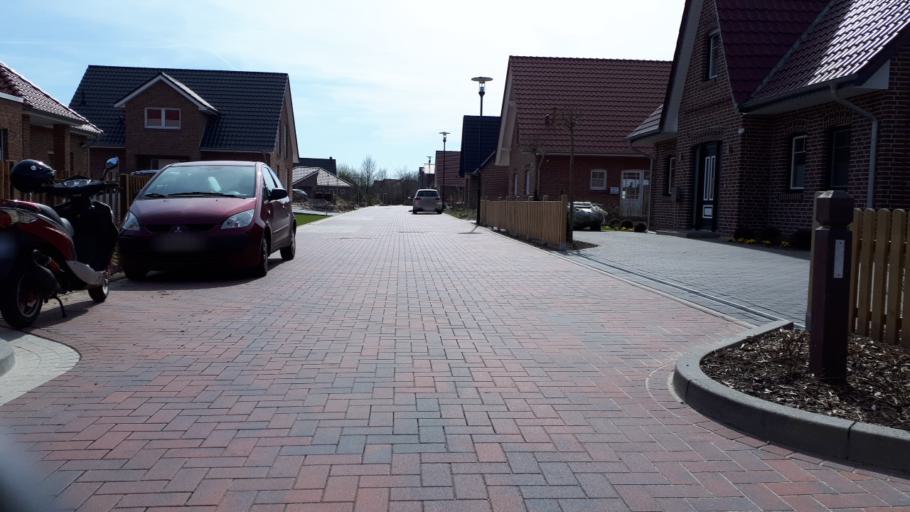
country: DE
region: Lower Saxony
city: Wardenburg
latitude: 53.0715
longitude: 8.1959
